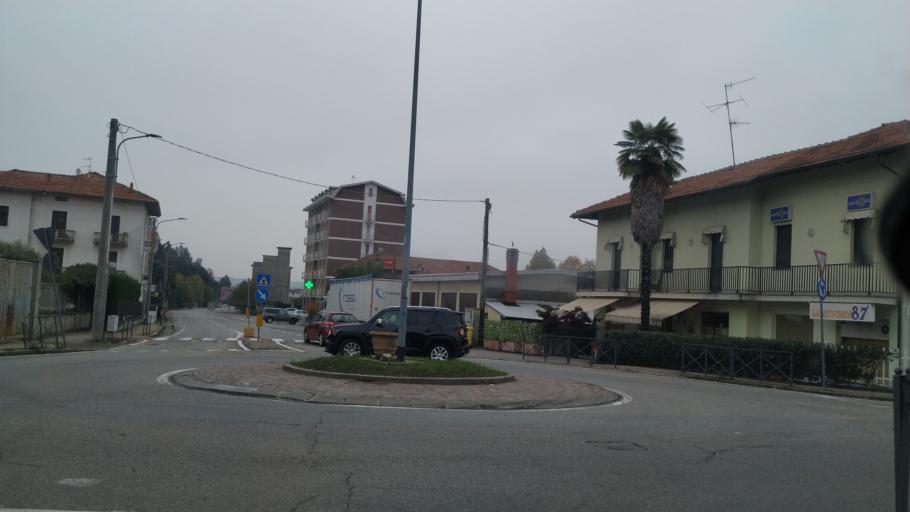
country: IT
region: Piedmont
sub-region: Provincia di Biella
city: Cossato
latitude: 45.5756
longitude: 8.1871
